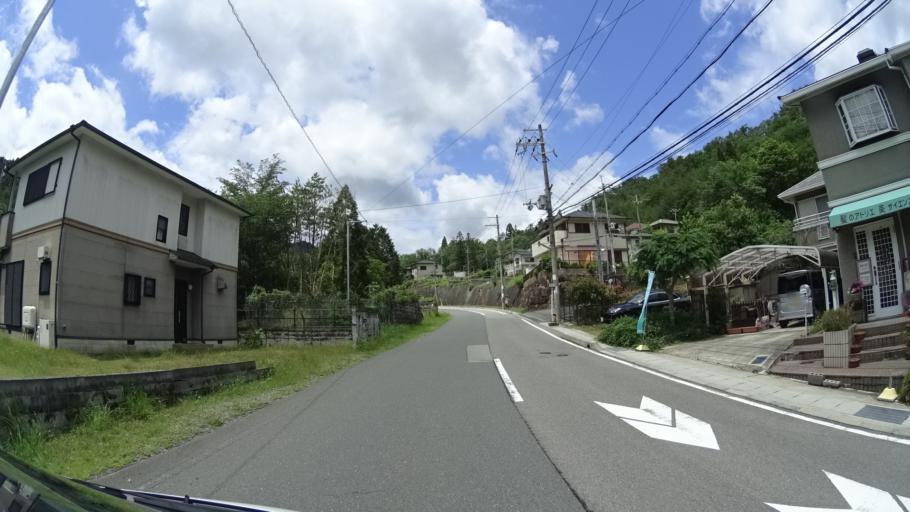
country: JP
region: Kyoto
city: Kameoka
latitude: 35.0174
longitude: 135.4184
